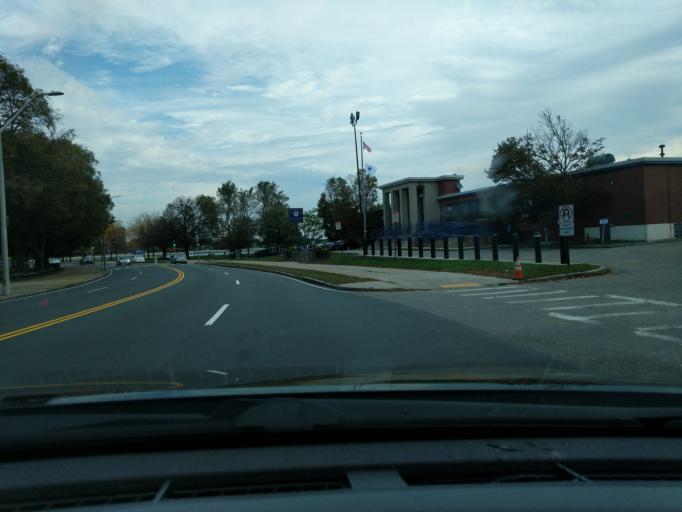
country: US
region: Massachusetts
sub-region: Suffolk County
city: South Boston
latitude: 42.3223
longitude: -71.0497
